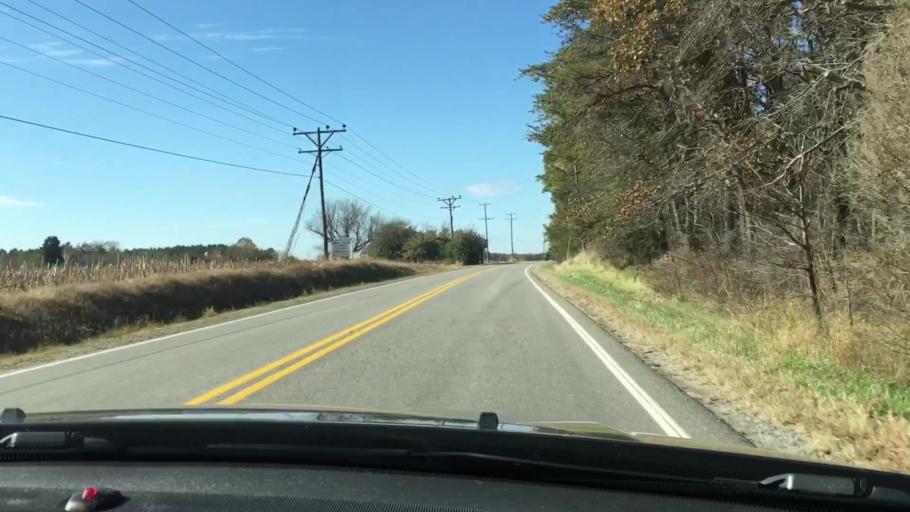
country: US
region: Virginia
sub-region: King William County
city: Central Garage
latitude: 37.7227
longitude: -77.0858
